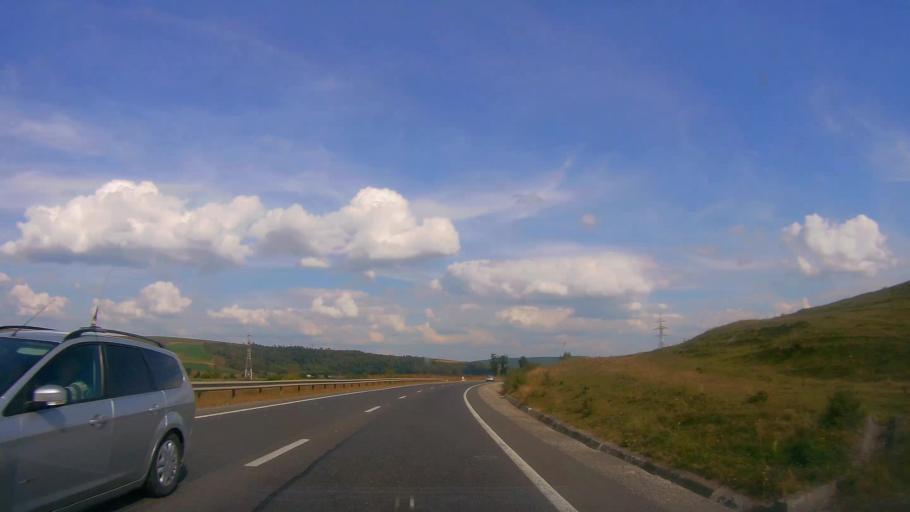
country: RO
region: Brasov
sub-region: Comuna Homorod
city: Homorod
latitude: 46.0368
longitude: 25.2443
